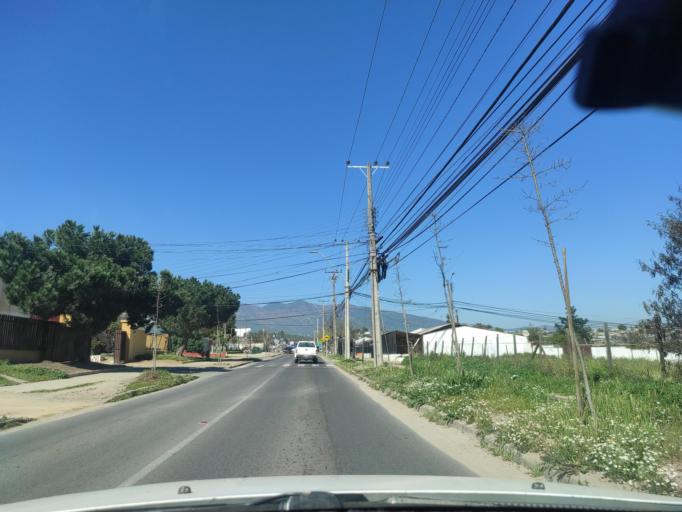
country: CL
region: Valparaiso
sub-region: Provincia de Marga Marga
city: Limache
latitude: -33.0128
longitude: -71.2534
